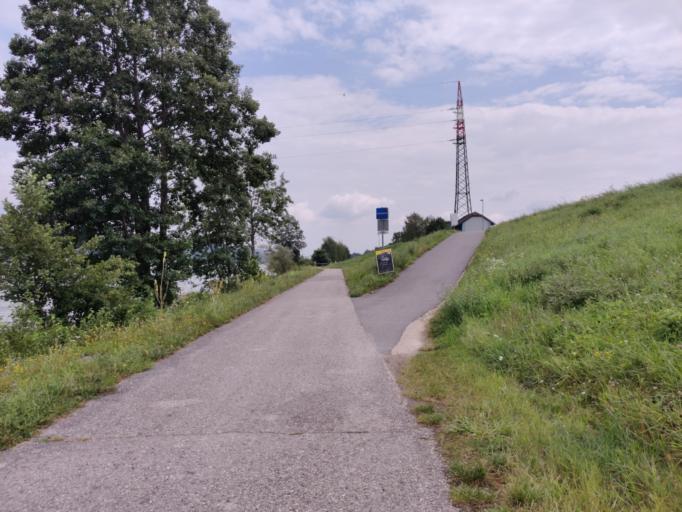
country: AT
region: Lower Austria
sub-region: Politischer Bezirk Melk
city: Marbach an der Donau
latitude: 48.2110
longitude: 15.1500
